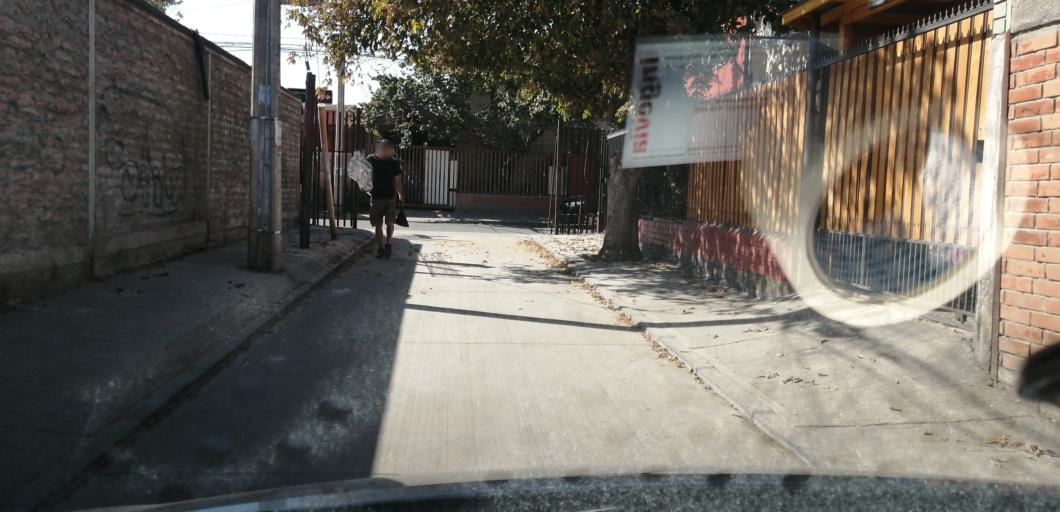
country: CL
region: Santiago Metropolitan
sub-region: Provincia de Santiago
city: Lo Prado
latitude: -33.4626
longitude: -70.7451
